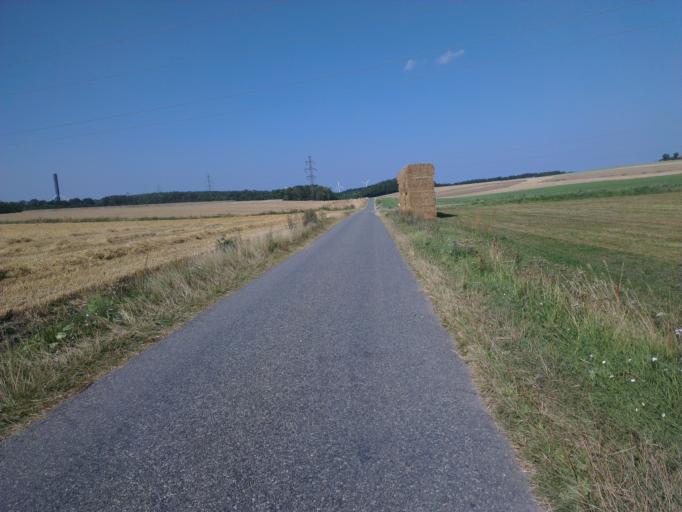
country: DK
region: Capital Region
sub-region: Frederikssund Kommune
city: Skibby
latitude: 55.8060
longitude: 11.9043
